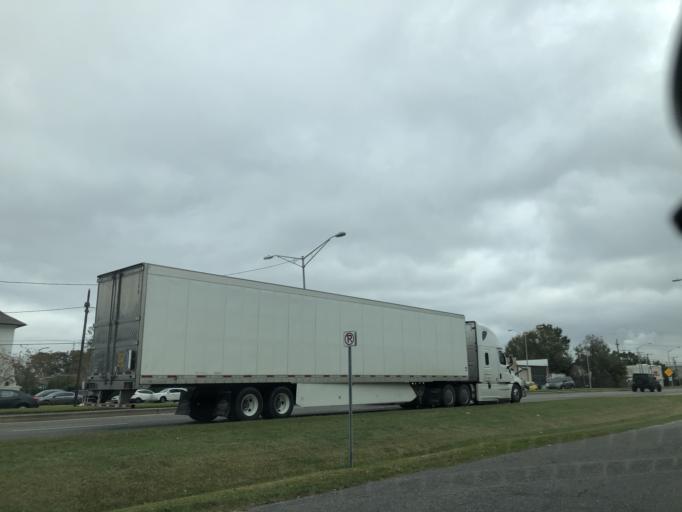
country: US
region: Louisiana
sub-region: Jefferson Parish
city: Metairie
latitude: 29.9797
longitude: -90.1565
